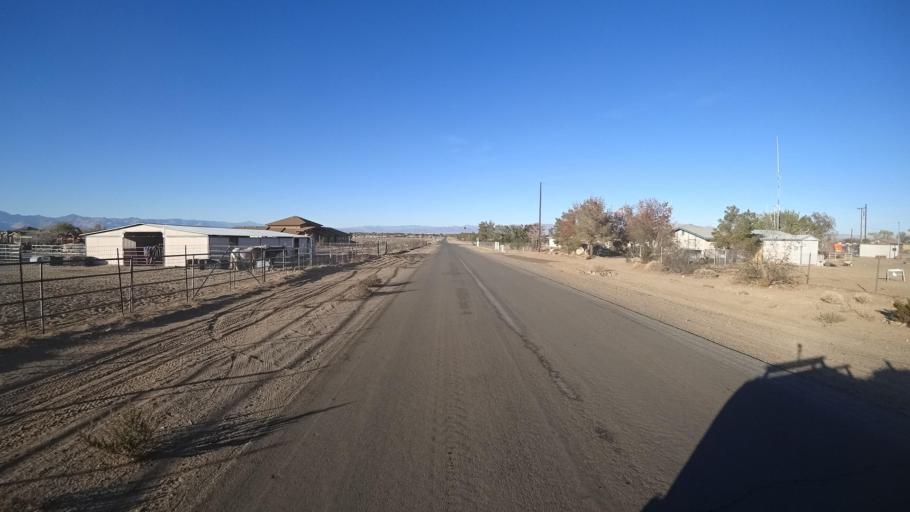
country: US
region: California
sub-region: Kern County
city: Ridgecrest
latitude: 35.5993
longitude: -117.6616
